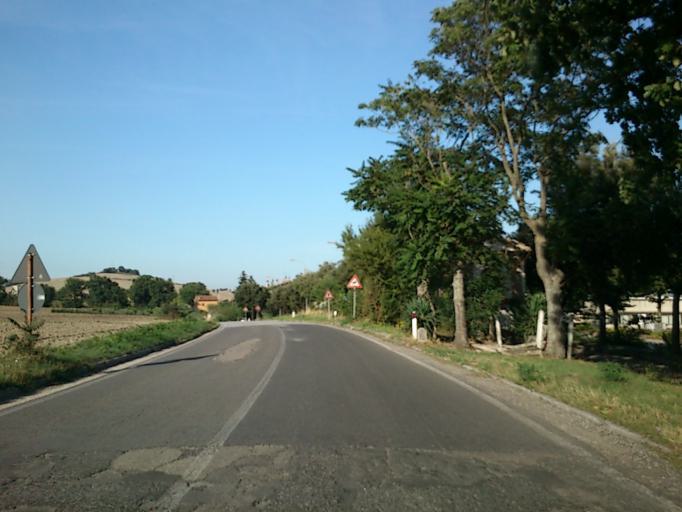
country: IT
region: The Marches
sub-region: Provincia di Pesaro e Urbino
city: Montefelcino
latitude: 43.7082
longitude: 12.8442
